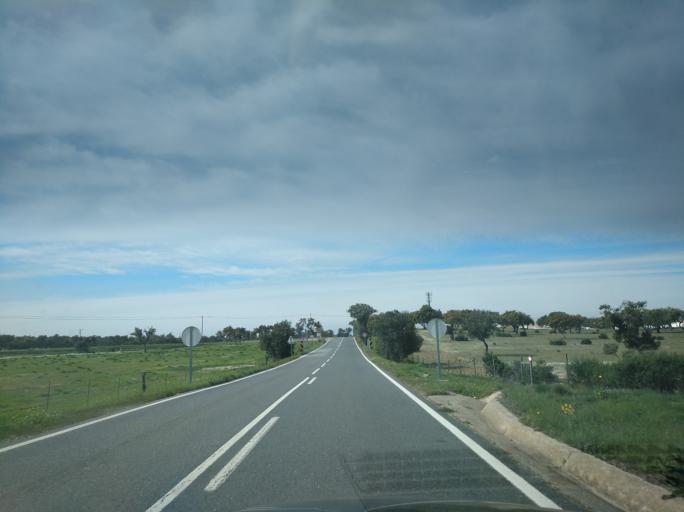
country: PT
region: Beja
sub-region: Mertola
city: Mertola
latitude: 37.7411
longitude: -7.7883
